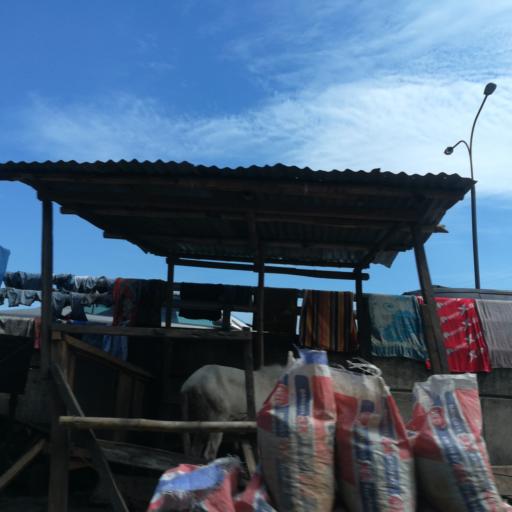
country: NG
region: Lagos
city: Lagos
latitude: 6.4656
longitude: 3.3894
